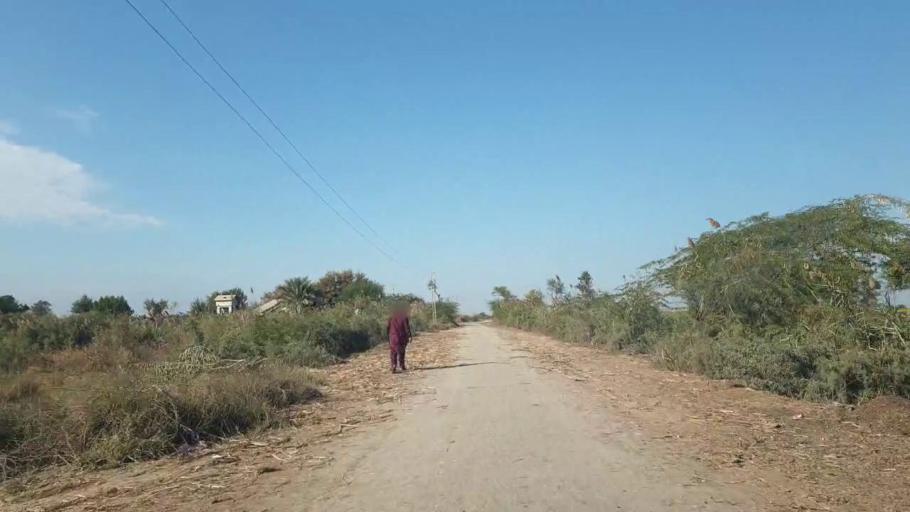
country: PK
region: Sindh
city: Sanghar
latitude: 26.0371
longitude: 68.8819
